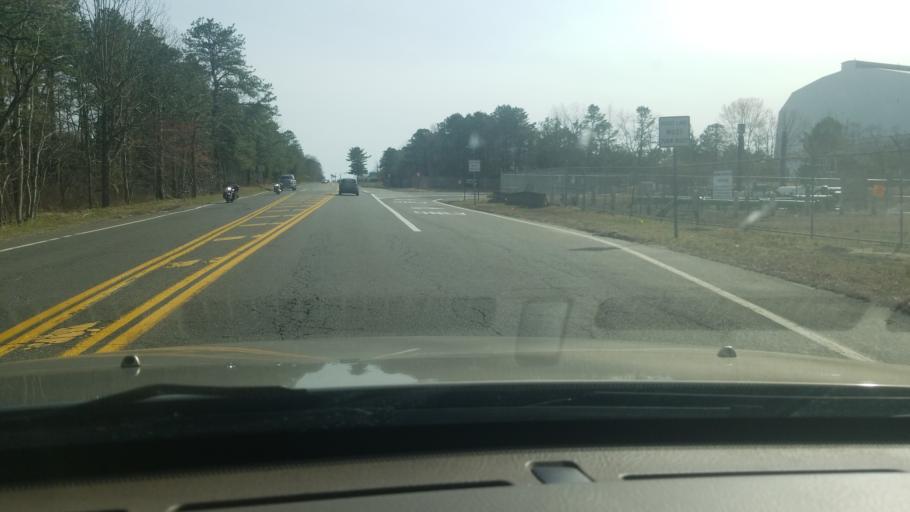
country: US
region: New Jersey
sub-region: Ocean County
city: Lakehurst
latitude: 40.0307
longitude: -74.3070
